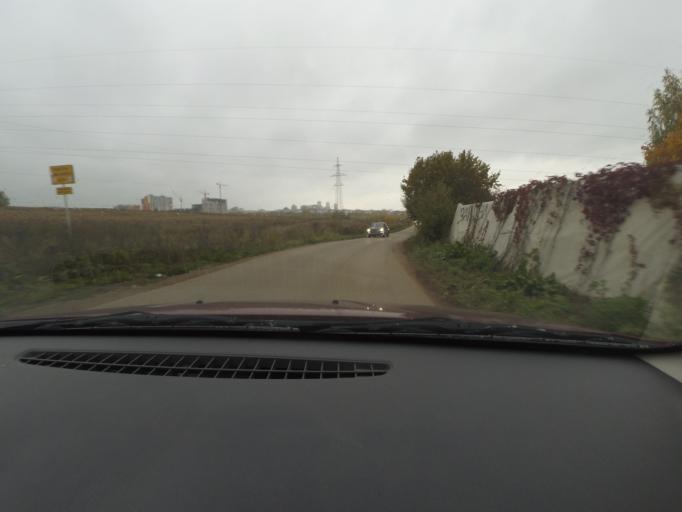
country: RU
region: Nizjnij Novgorod
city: Afonino
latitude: 56.2720
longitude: 44.0580
